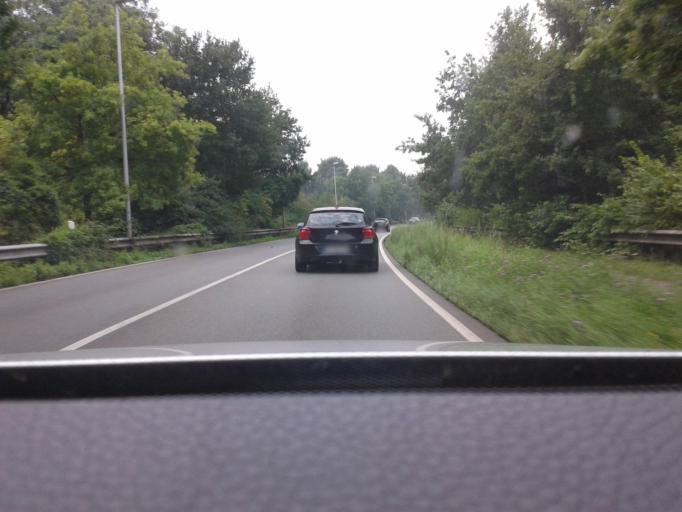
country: DE
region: North Rhine-Westphalia
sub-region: Regierungsbezirk Dusseldorf
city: Hochfeld
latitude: 51.4333
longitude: 6.7084
